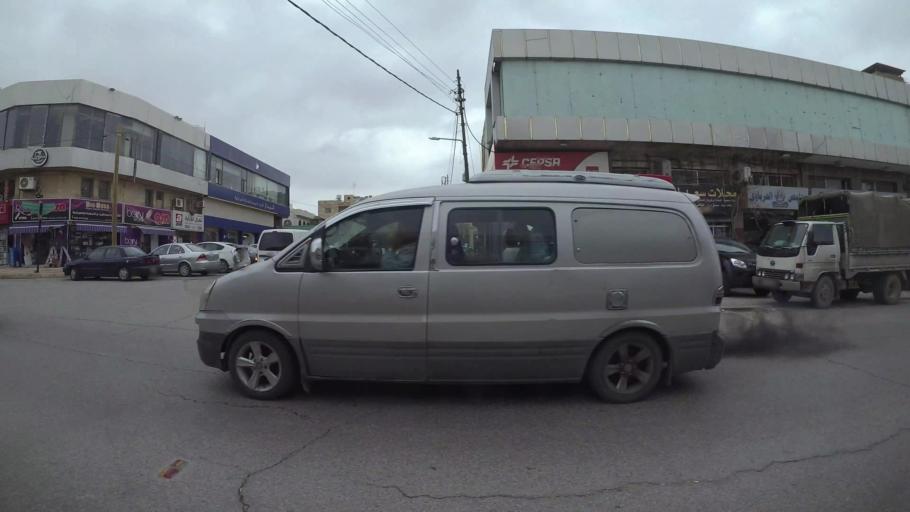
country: JO
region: Amman
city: Wadi as Sir
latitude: 31.9828
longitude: 35.8477
